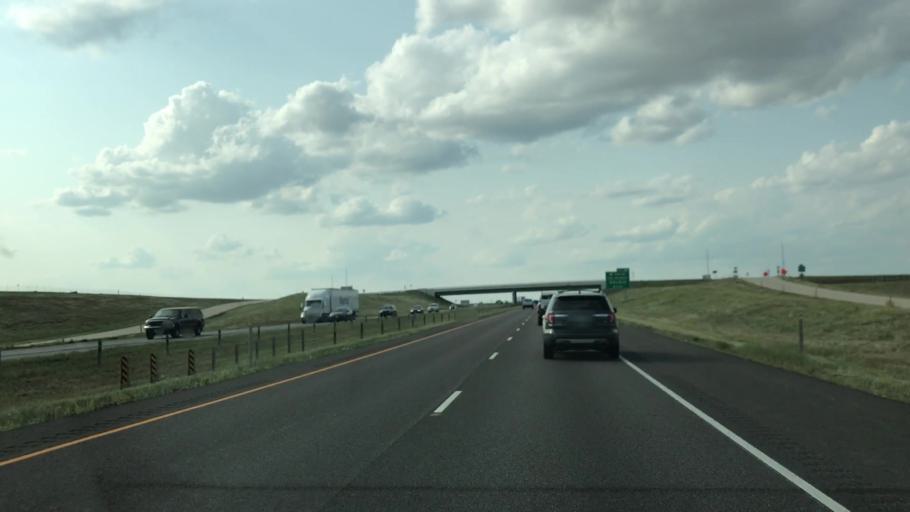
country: US
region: Colorado
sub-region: Adams County
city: Aurora
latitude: 39.8098
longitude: -104.7189
